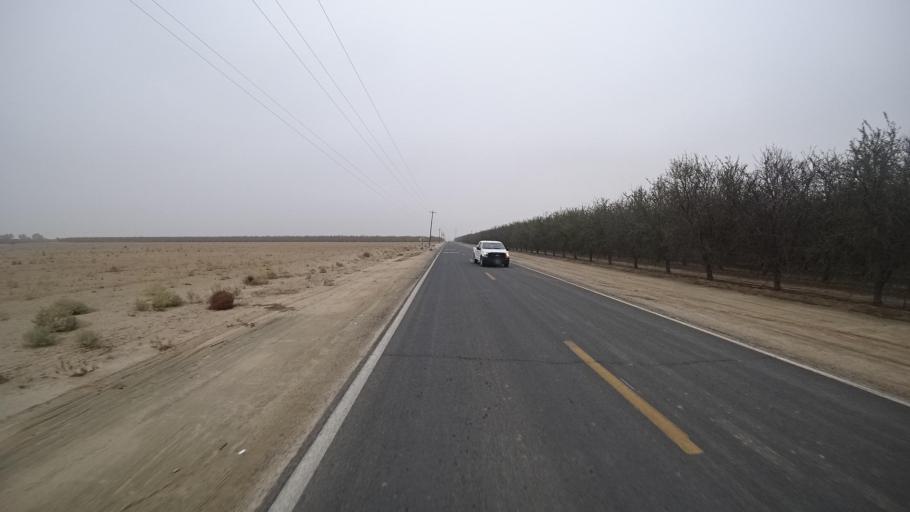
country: US
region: California
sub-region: Kern County
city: Lost Hills
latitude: 35.6090
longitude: -119.5804
